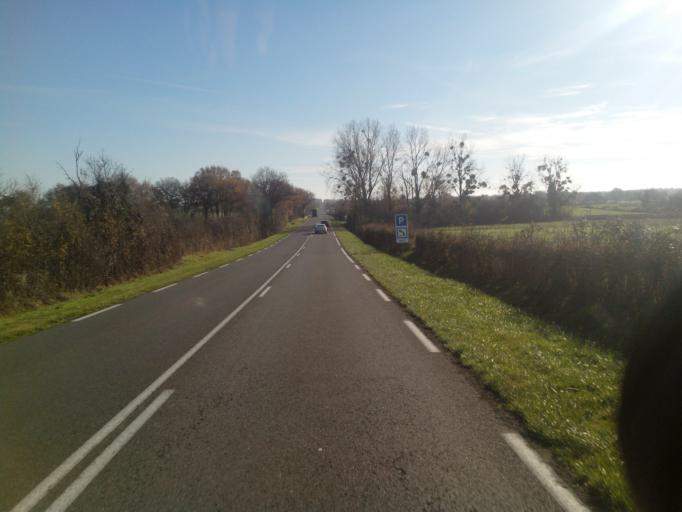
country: FR
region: Poitou-Charentes
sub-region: Departement de la Vienne
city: Lussac-les-Chateaux
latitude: 46.3751
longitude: 0.7580
